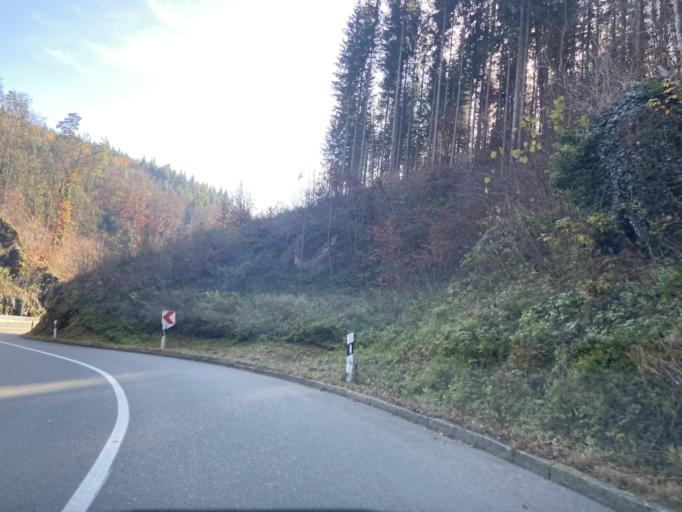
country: DE
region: Baden-Wuerttemberg
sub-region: Tuebingen Region
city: Stetten am Kalten Markt
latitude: 48.0996
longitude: 9.0928
